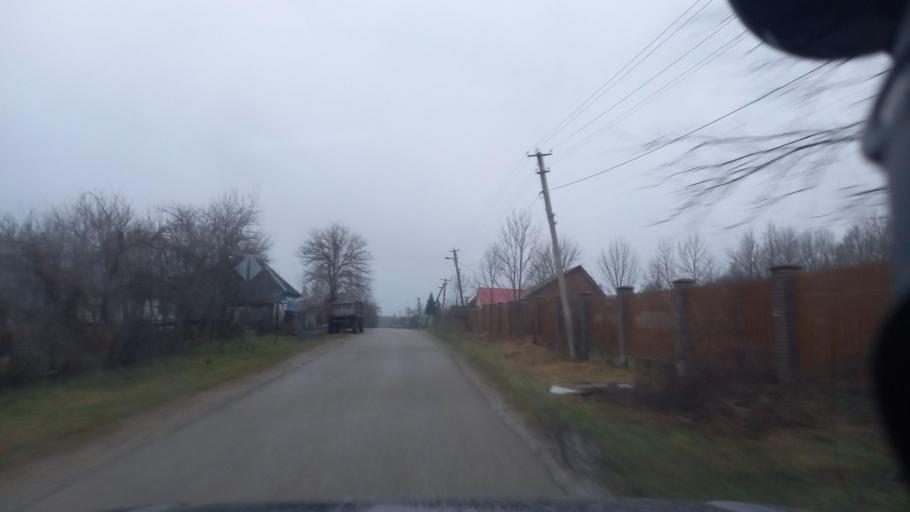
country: RU
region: Krasnodarskiy
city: Saratovskaya
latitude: 44.6481
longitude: 39.3155
